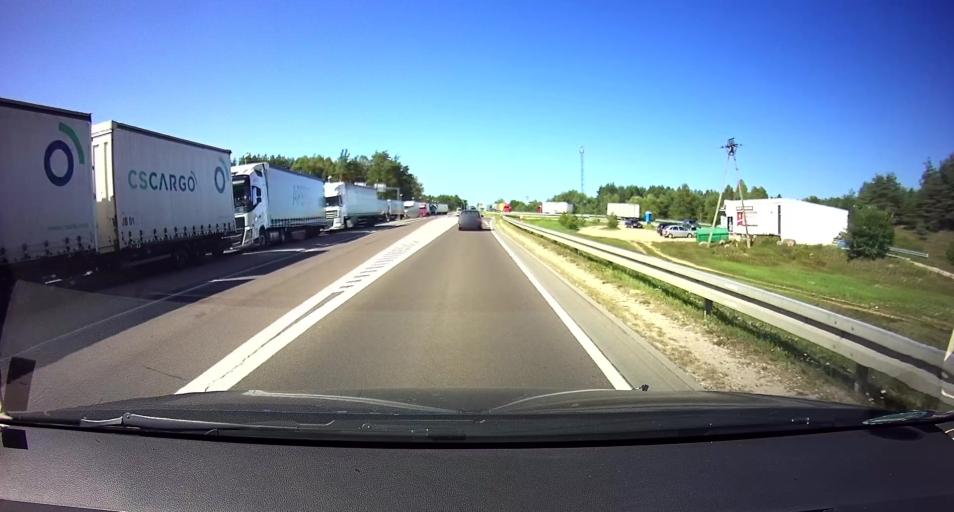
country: BY
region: Grodnenskaya
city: Vyalikaya Byerastavitsa
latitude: 53.1242
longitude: 23.8757
